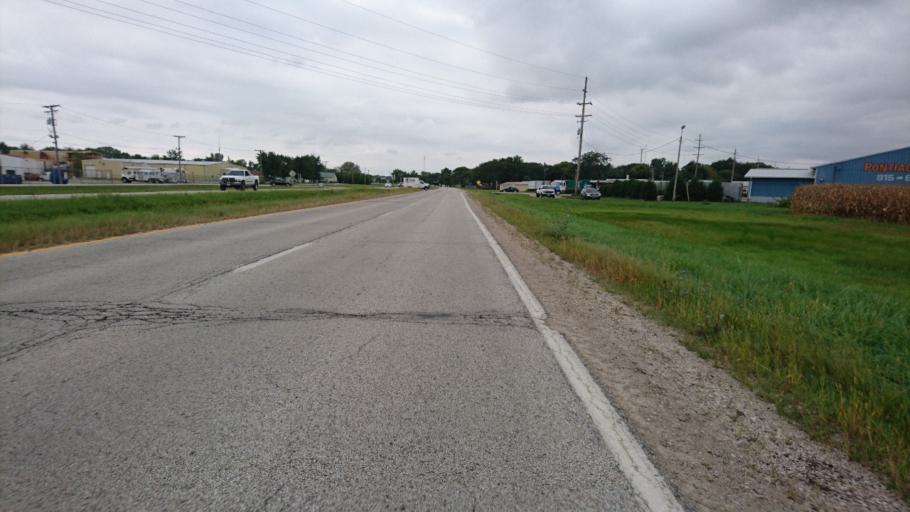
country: US
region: Illinois
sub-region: Livingston County
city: Pontiac
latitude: 40.8929
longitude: -88.6346
